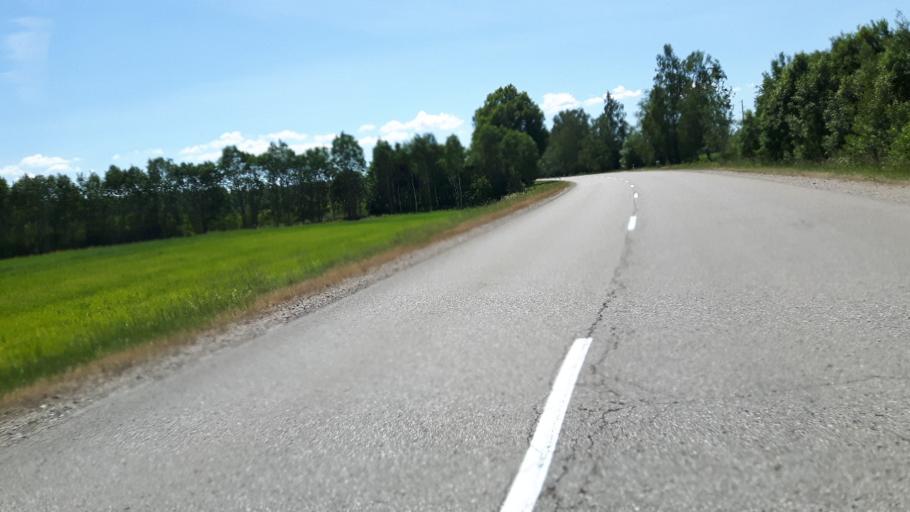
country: LV
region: Kuldigas Rajons
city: Kuldiga
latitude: 56.8999
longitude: 21.8897
